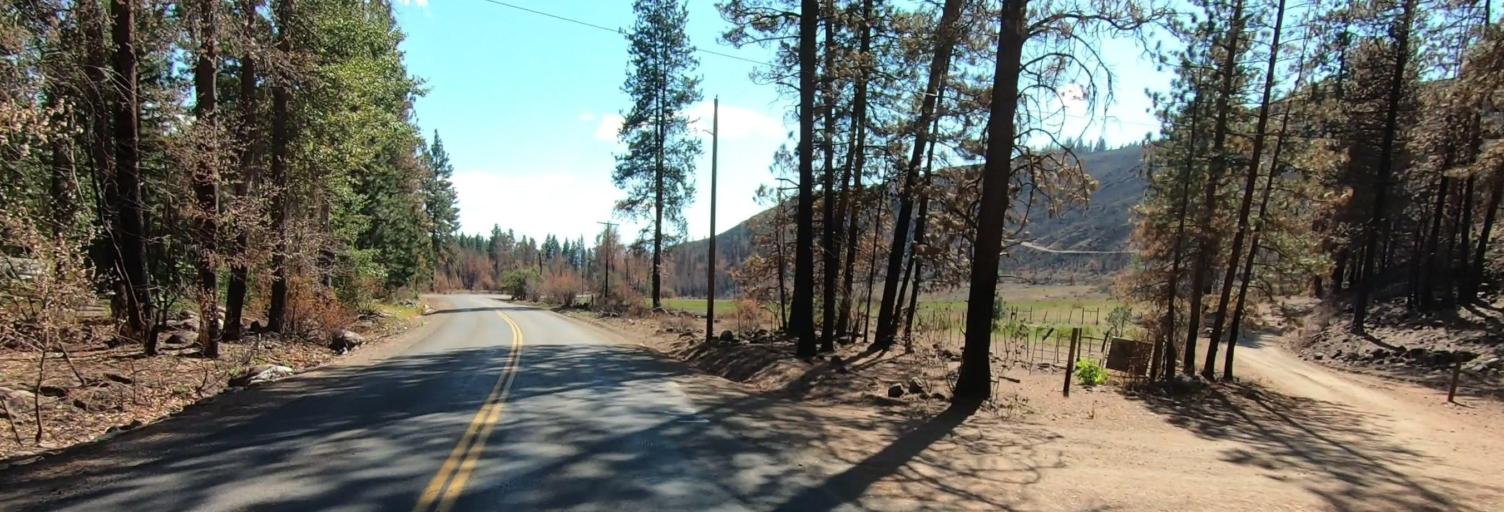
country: US
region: Washington
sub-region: Okanogan County
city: Brewster
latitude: 48.5692
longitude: -120.1777
